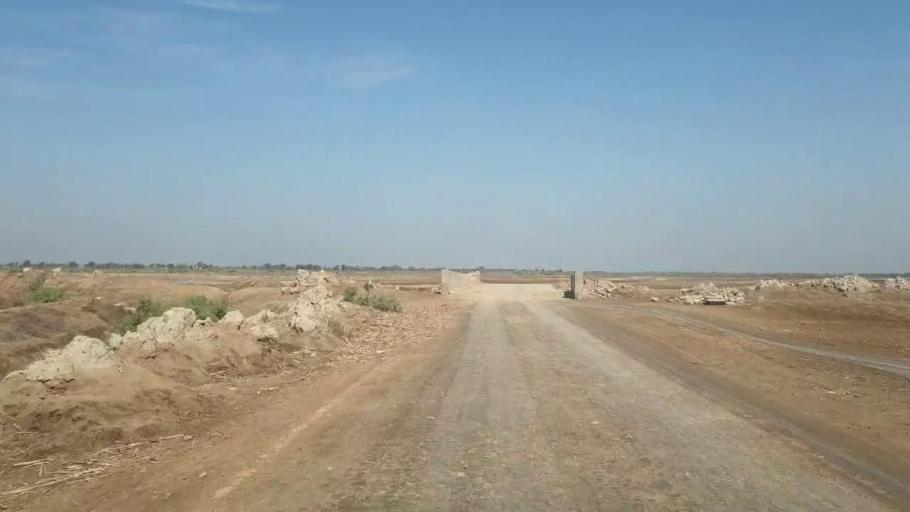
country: PK
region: Sindh
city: Samaro
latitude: 25.3584
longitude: 69.2539
